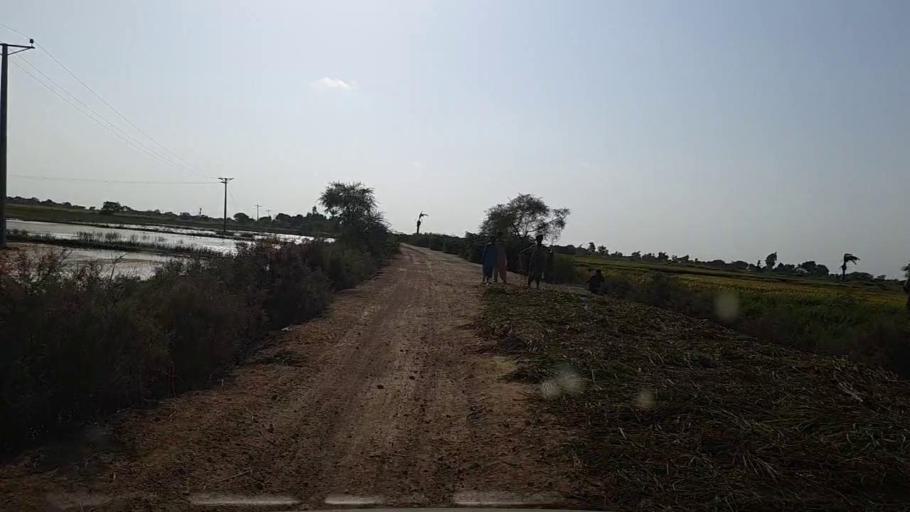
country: PK
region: Sindh
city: Kario
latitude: 24.8054
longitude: 68.5145
